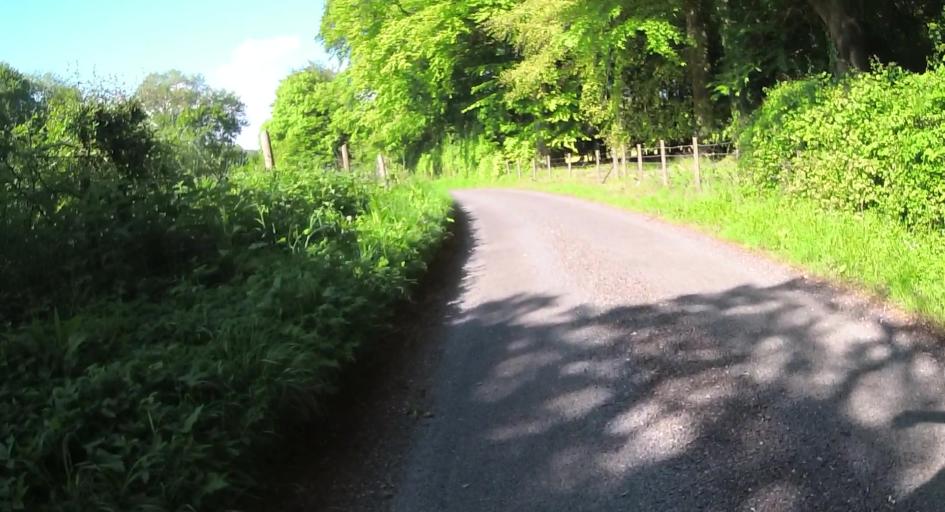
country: GB
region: England
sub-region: Hampshire
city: Overton
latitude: 51.1731
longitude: -1.2163
